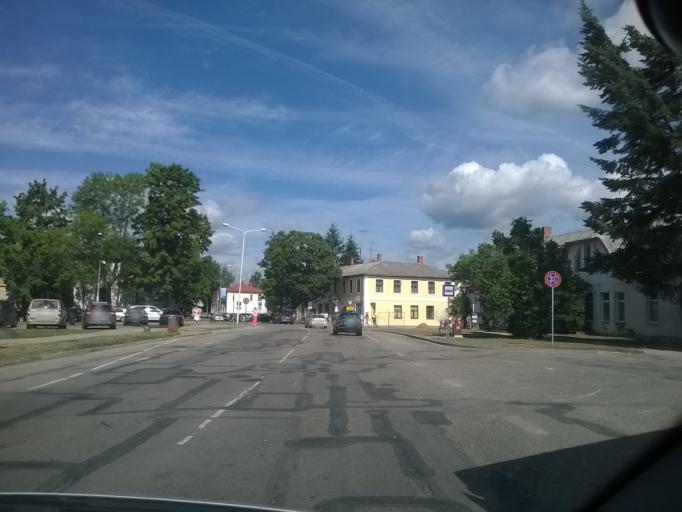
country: LV
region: Aluksnes Rajons
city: Aluksne
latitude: 57.4203
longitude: 27.0517
